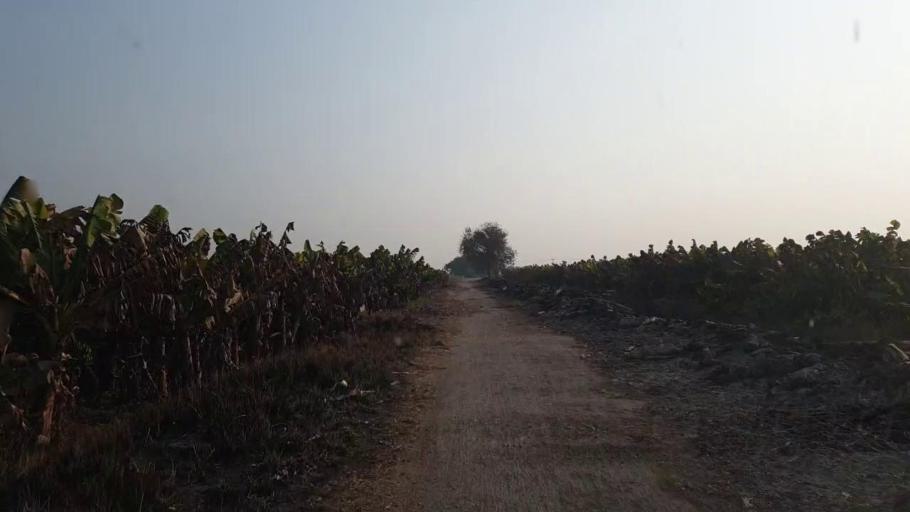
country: PK
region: Sindh
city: Hala
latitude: 25.8859
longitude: 68.4498
